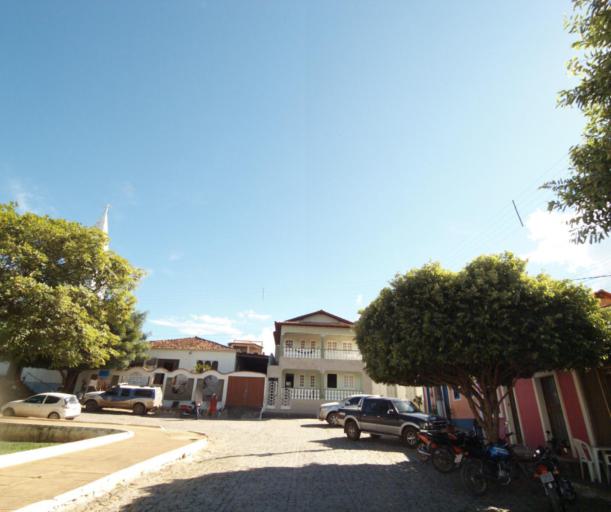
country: BR
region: Bahia
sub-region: Correntina
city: Correntina
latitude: -13.3412
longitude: -44.6376
